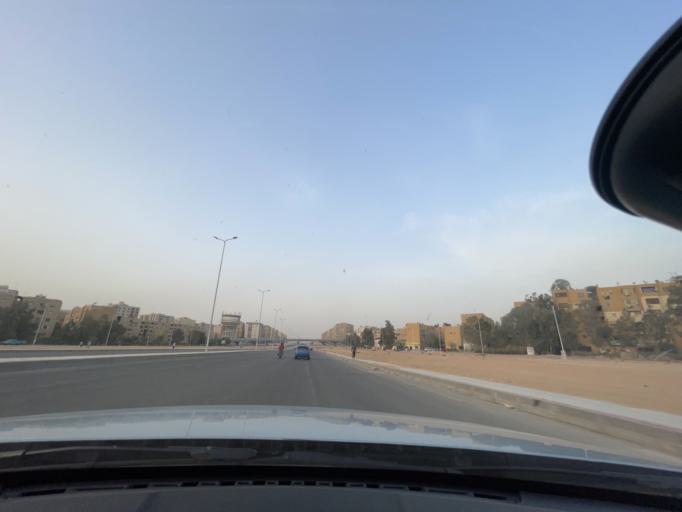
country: EG
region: Muhafazat al Qahirah
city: Cairo
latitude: 30.0444
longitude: 31.3629
